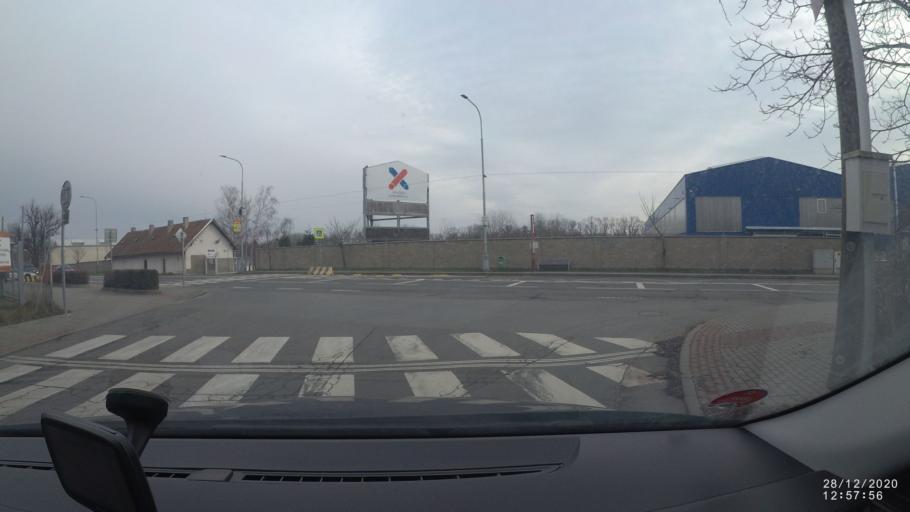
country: CZ
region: Praha
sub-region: Praha 19
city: Satalice
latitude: 50.1519
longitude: 14.5908
